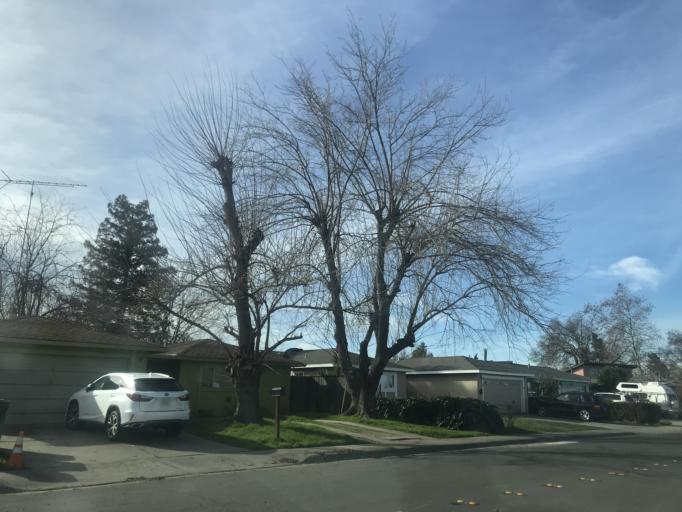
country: US
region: California
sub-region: Yolo County
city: Woodland
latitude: 38.6670
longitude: -121.7596
